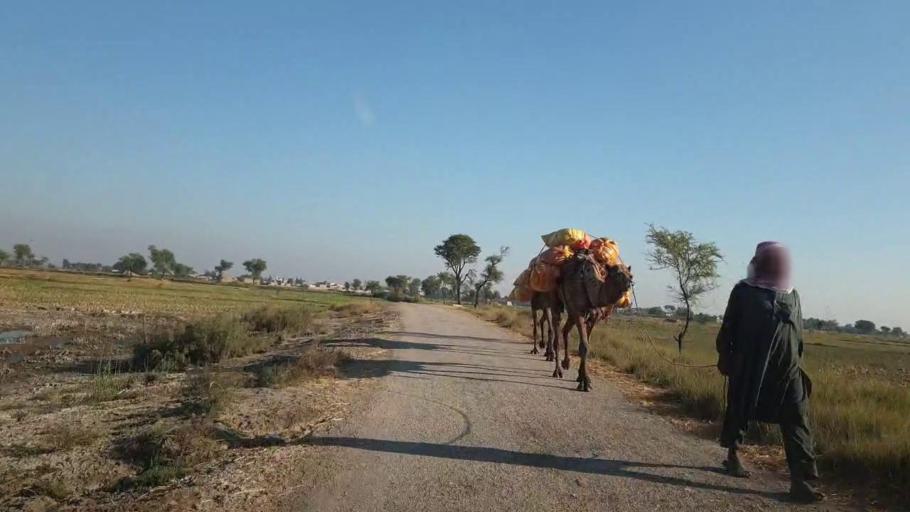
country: PK
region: Sindh
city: Phulji
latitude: 26.9883
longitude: 67.6893
